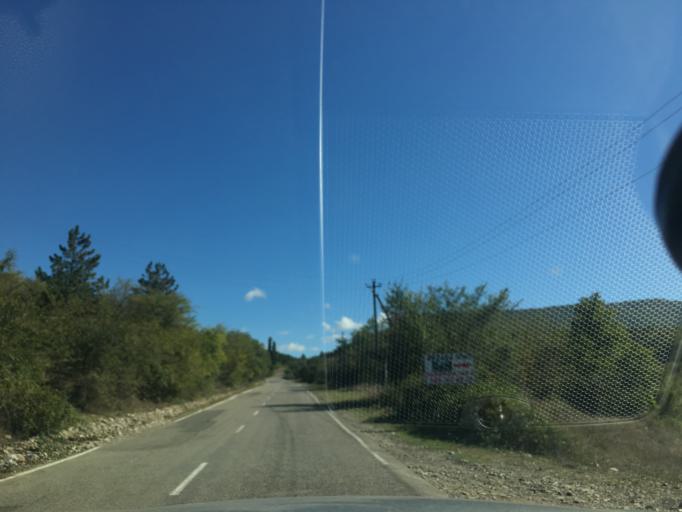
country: GE
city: Zahesi
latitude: 41.8286
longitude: 44.8507
